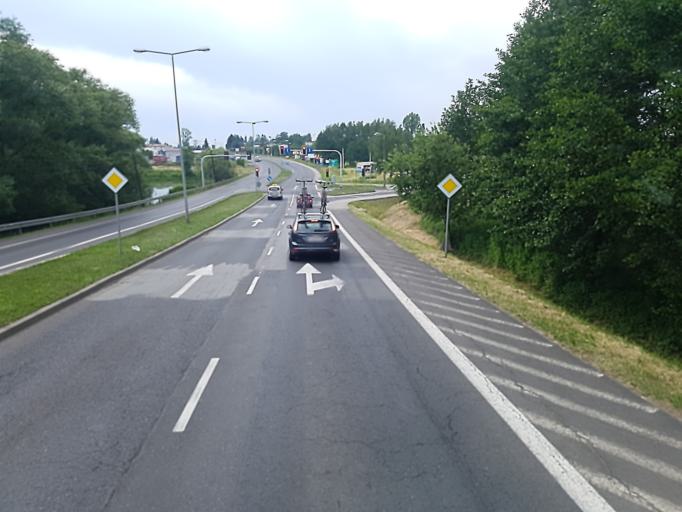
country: PL
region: Silesian Voivodeship
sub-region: Powiat pszczynski
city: Krzyzowice
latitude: 49.9588
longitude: 18.6705
